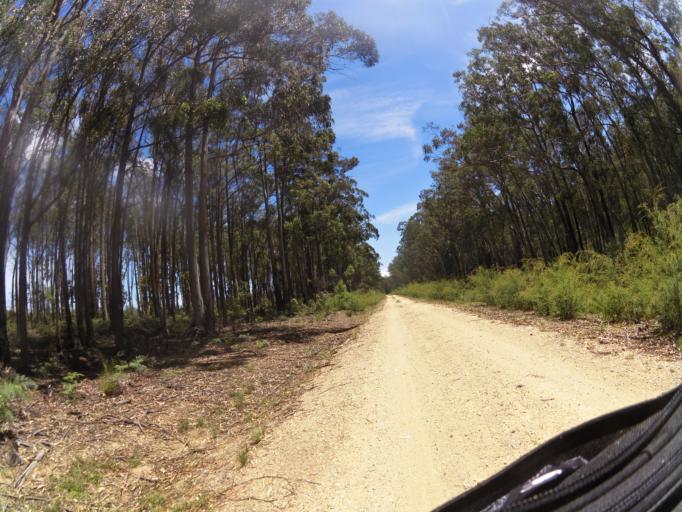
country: AU
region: Victoria
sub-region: East Gippsland
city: Lakes Entrance
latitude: -37.7532
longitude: 147.9191
